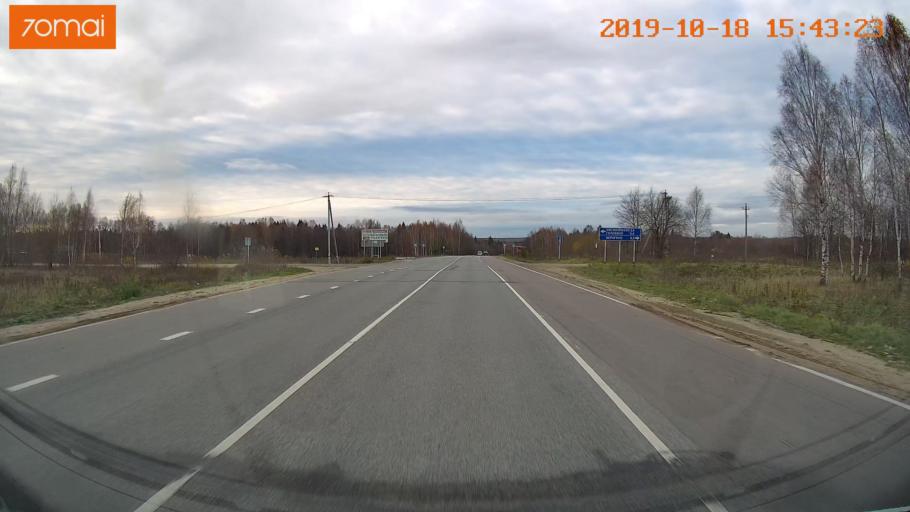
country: RU
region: Vladimir
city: Golovino
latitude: 55.9668
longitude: 40.5518
